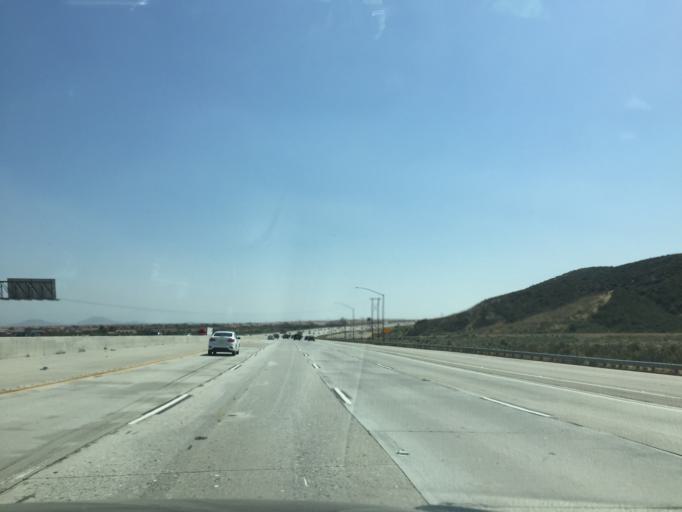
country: US
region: California
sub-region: San Bernardino County
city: Muscoy
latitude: 34.1998
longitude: -117.4172
